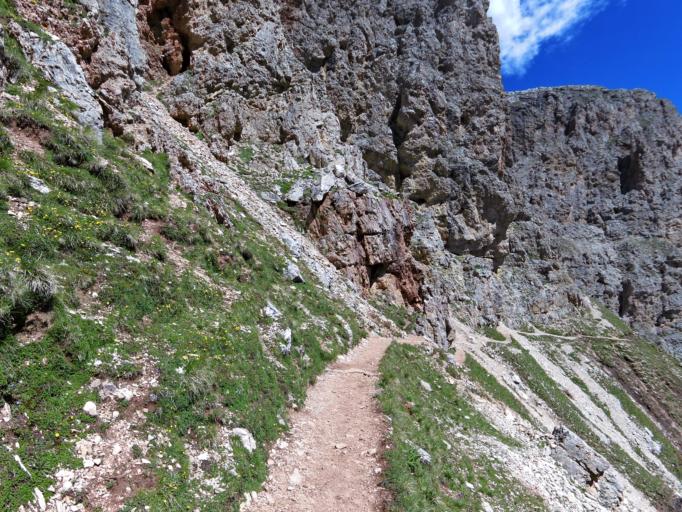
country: IT
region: Trentino-Alto Adige
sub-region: Bolzano
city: Siusi
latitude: 46.4965
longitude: 11.6146
